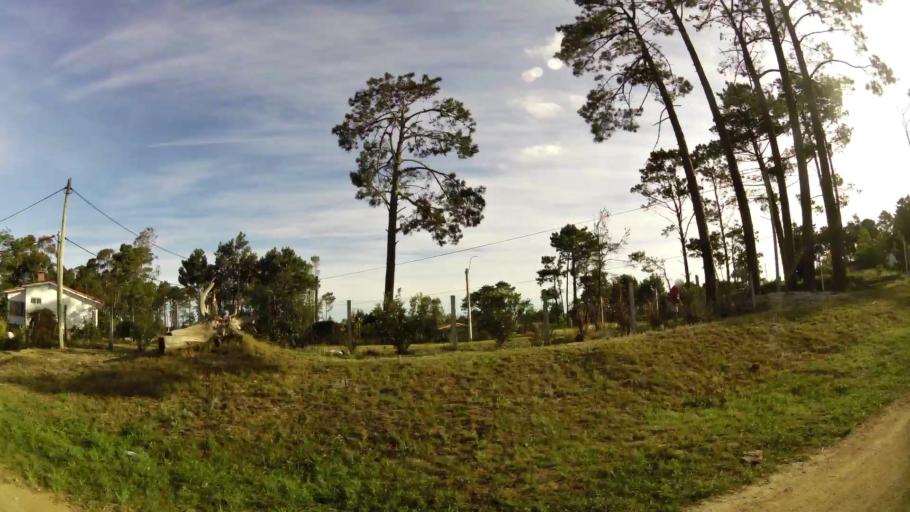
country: UY
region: Canelones
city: Empalme Olmos
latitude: -34.7793
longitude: -55.8589
